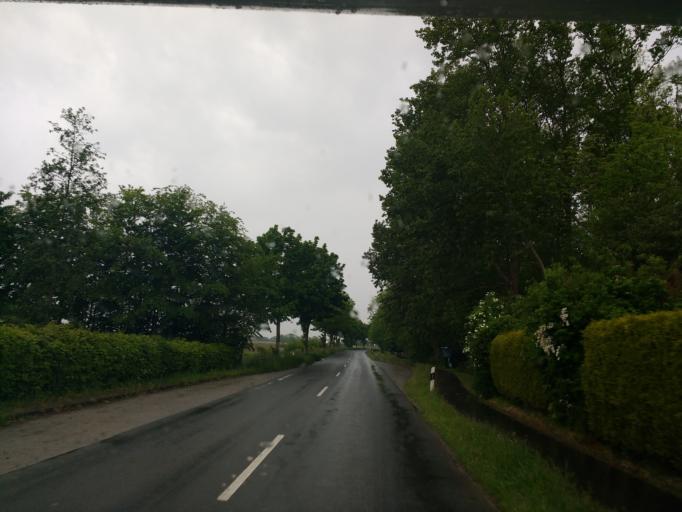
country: DE
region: Lower Saxony
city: Schillig
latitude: 53.7065
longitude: 7.9530
